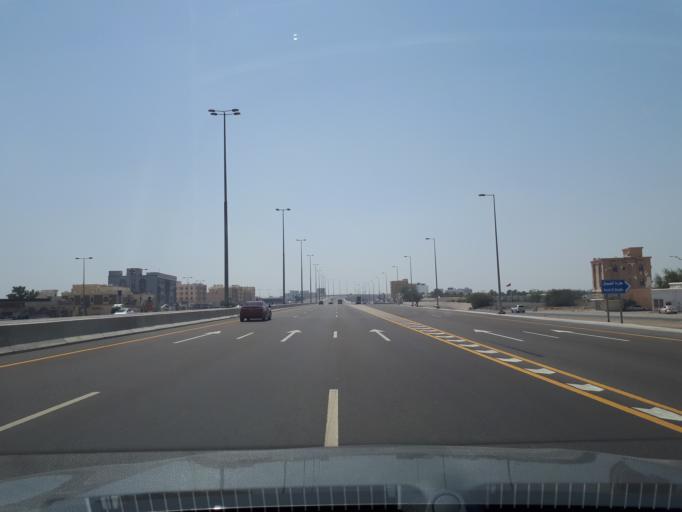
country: OM
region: Al Batinah
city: Al Liwa'
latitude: 24.4207
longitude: 56.6202
